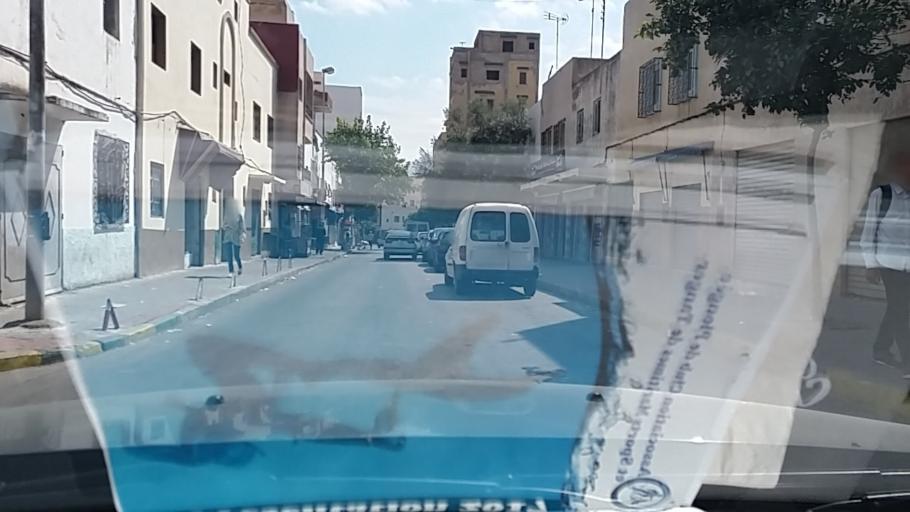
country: MA
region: Tanger-Tetouan
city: Tetouan
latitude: 35.5710
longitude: -5.3562
